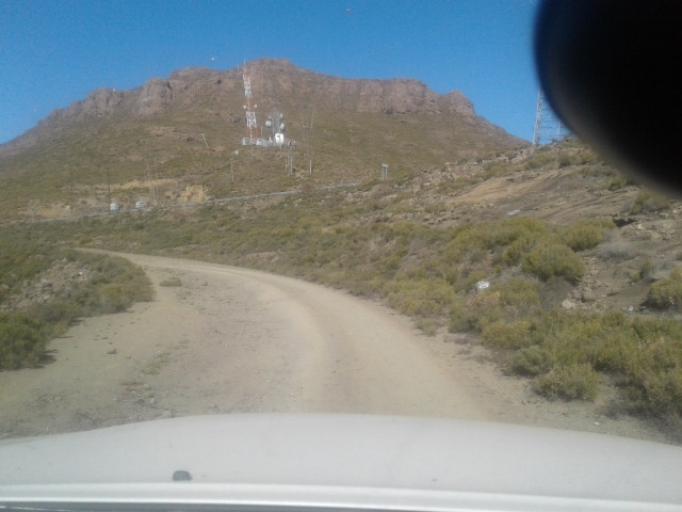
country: LS
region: Maseru
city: Nako
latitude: -29.4304
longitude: 27.9677
